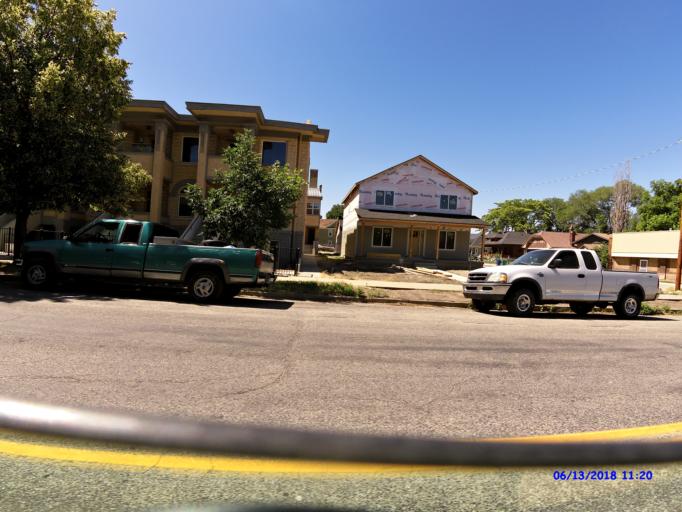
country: US
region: Utah
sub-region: Weber County
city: Ogden
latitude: 41.2205
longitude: -111.9548
